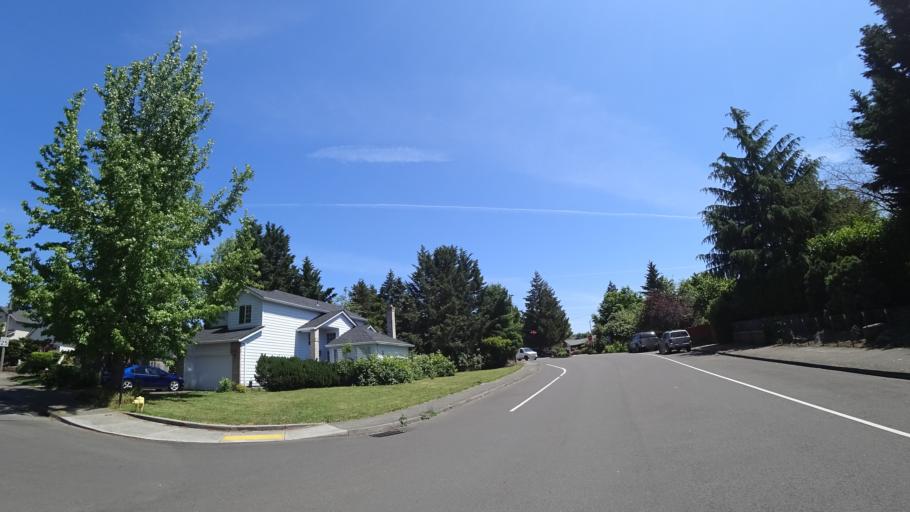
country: US
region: Oregon
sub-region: Washington County
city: Tigard
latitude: 45.4388
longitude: -122.8013
